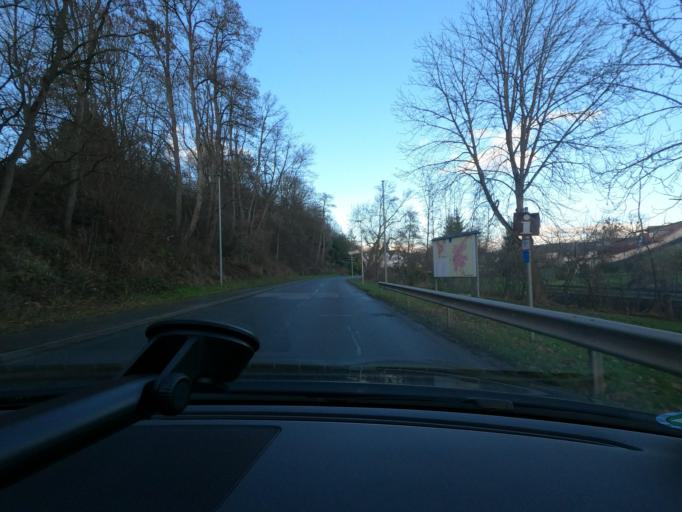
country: DE
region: Lower Saxony
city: Rhumspringe
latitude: 51.5833
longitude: 10.2940
